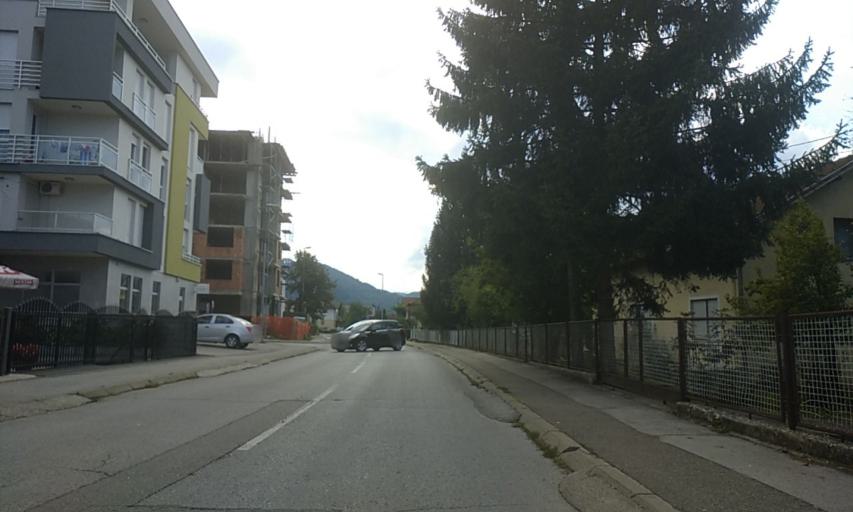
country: BA
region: Republika Srpska
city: Mejdan - Obilicevo
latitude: 44.7590
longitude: 17.1867
